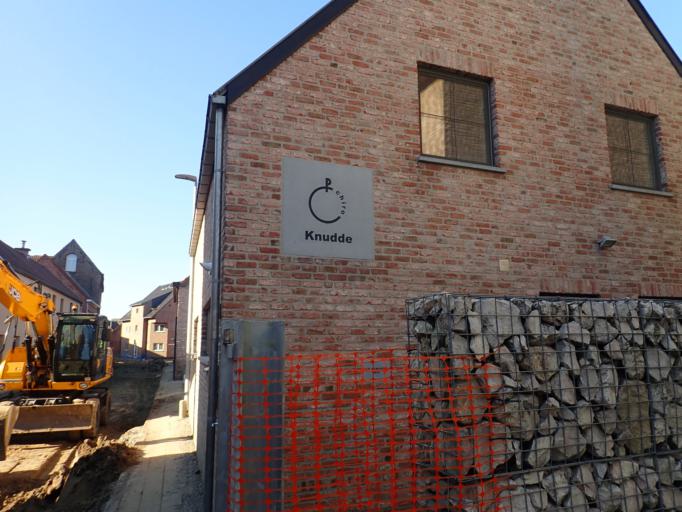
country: BE
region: Flanders
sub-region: Provincie Oost-Vlaanderen
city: Hamme
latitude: 51.0644
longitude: 4.1517
